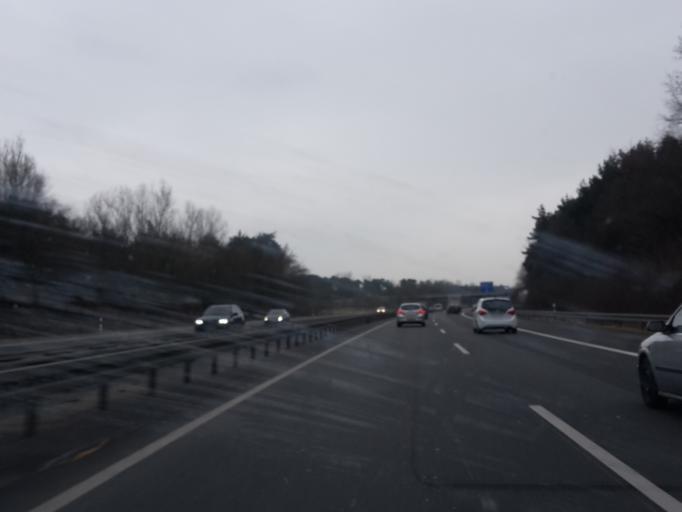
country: DE
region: Hesse
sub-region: Regierungsbezirk Darmstadt
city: Bickenbach
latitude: 49.7794
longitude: 8.6163
